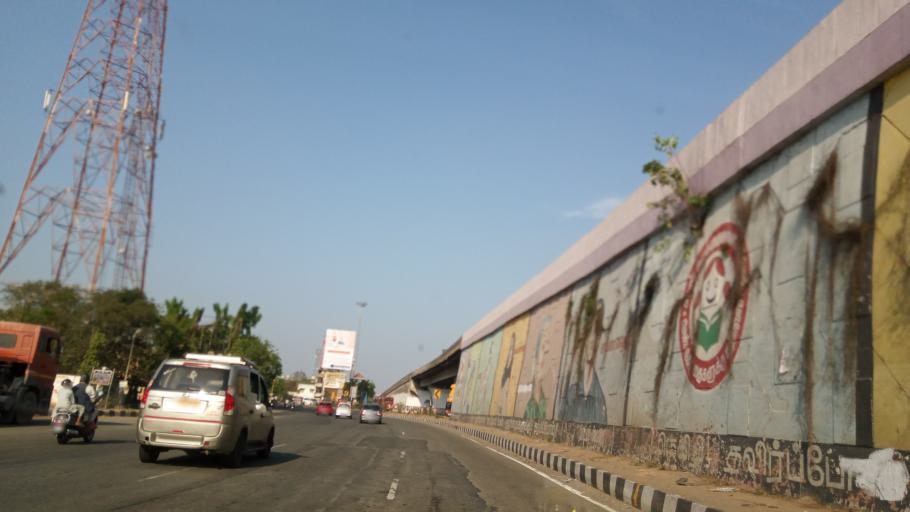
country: IN
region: Tamil Nadu
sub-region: Kancheepuram
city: Poonamalle
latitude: 13.0491
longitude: 80.0870
